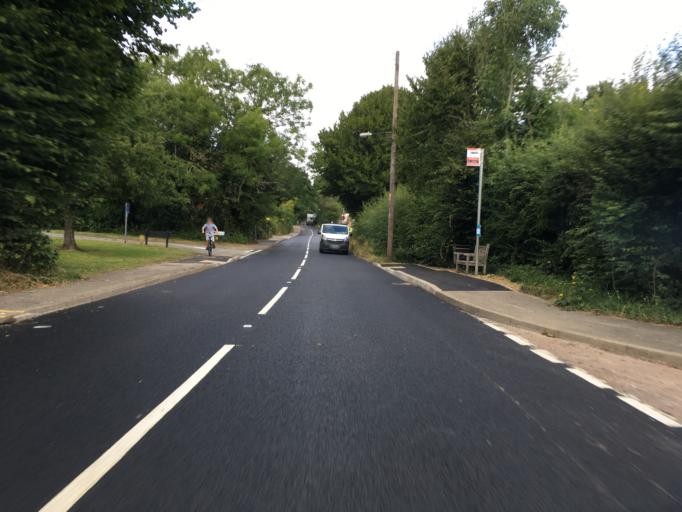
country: GB
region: England
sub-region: Kent
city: Cranbrook
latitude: 51.1109
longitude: 0.5587
